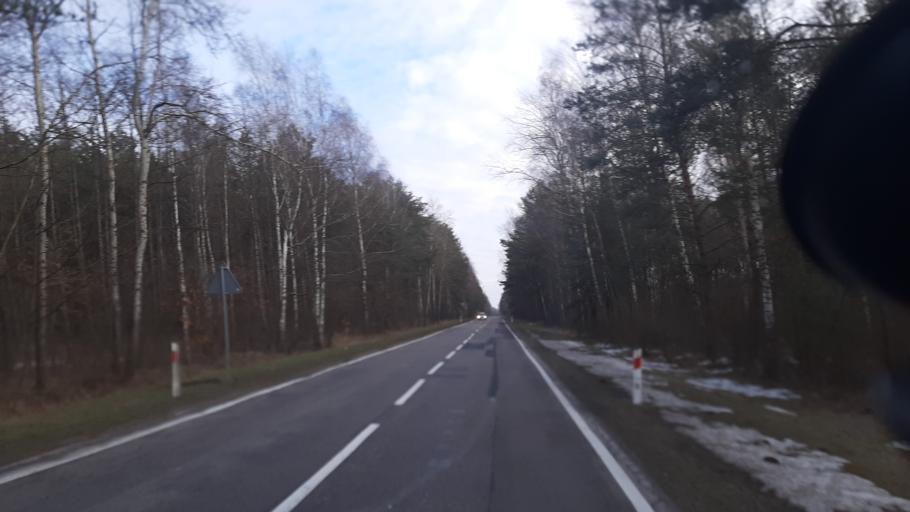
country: PL
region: Lublin Voivodeship
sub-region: Powiat lubartowski
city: Ostrow Lubelski
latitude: 51.4906
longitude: 22.8025
